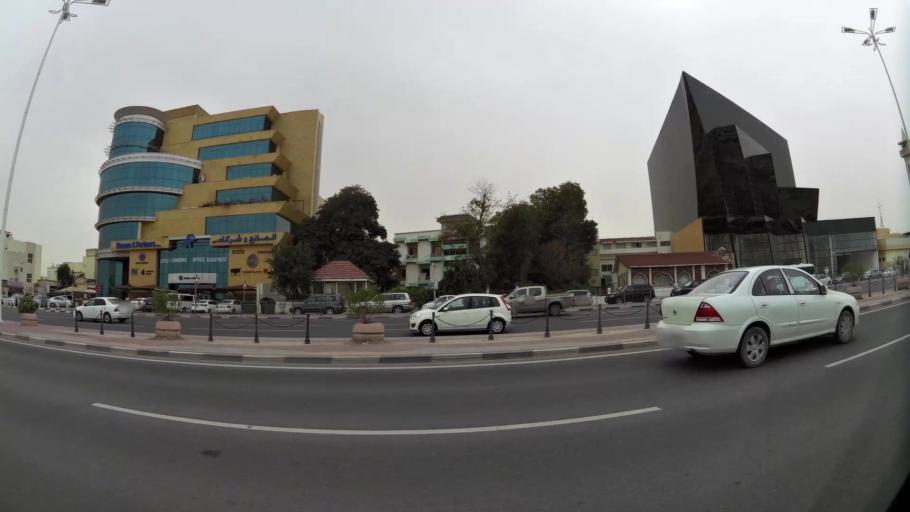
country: QA
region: Baladiyat ad Dawhah
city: Doha
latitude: 25.3040
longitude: 51.4996
